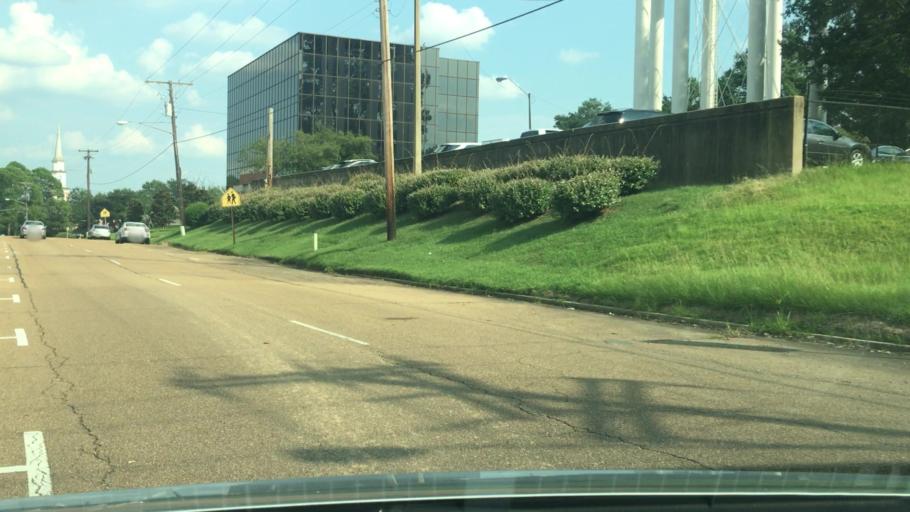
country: US
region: Mississippi
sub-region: Hinds County
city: Jackson
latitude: 32.3237
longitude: -90.1766
